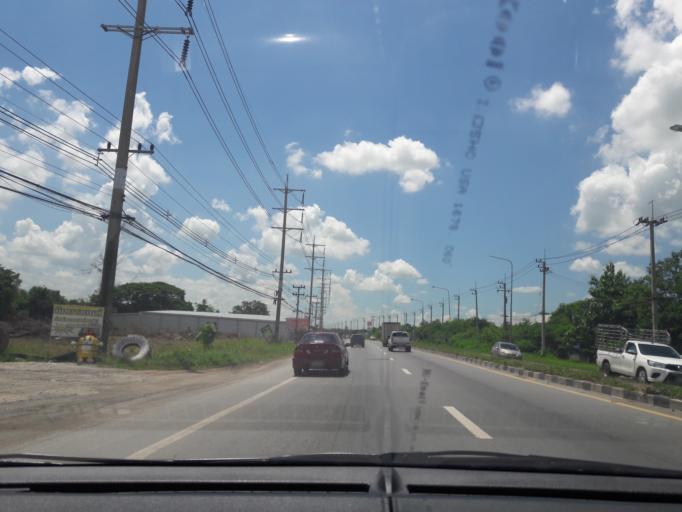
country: TH
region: Nakhon Pathom
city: Kamphaeng Saen
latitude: 14.0160
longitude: 100.0189
